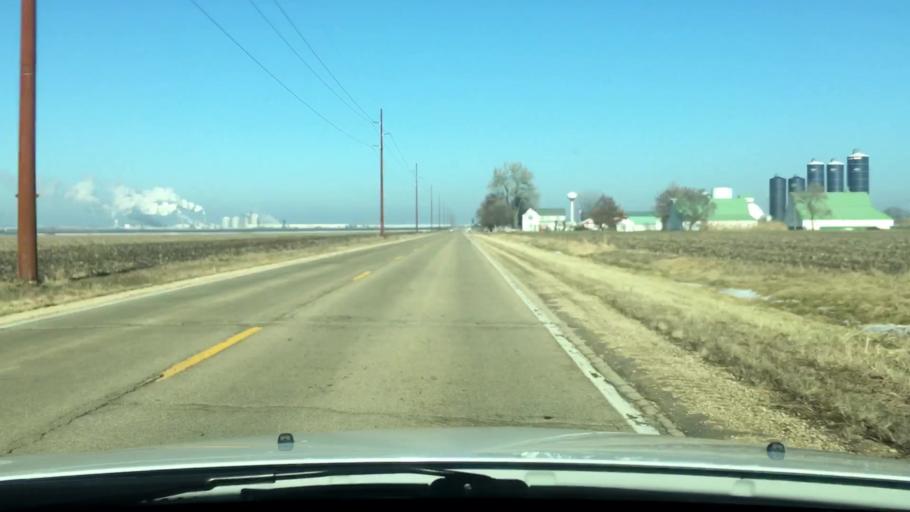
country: US
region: Illinois
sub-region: Ogle County
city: Rochelle
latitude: 41.8682
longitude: -89.0250
